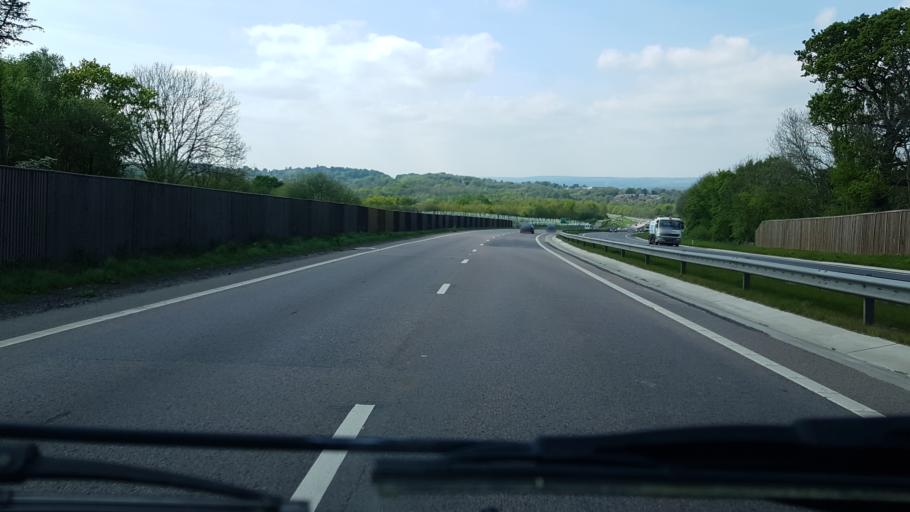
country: GB
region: England
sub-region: Kent
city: Tonbridge
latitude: 51.1749
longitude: 0.2966
